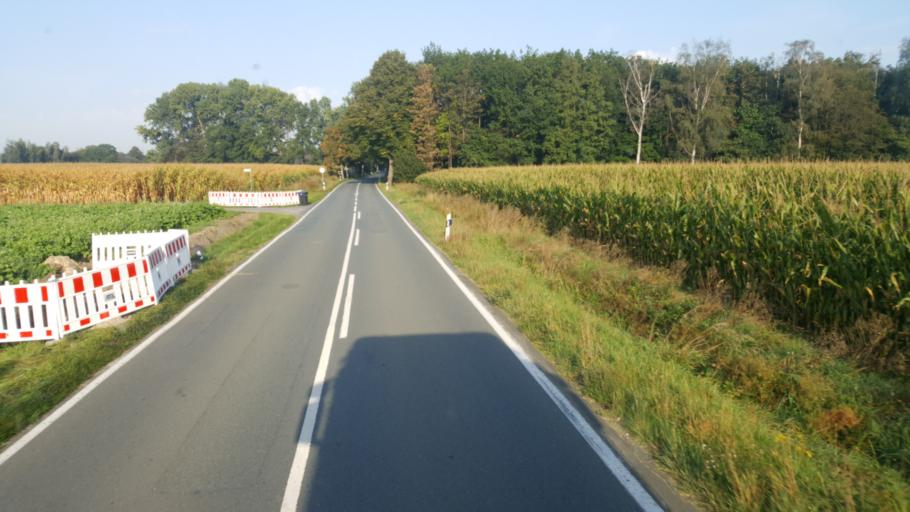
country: DE
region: North Rhine-Westphalia
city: Rietberg
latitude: 51.7418
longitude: 8.3894
